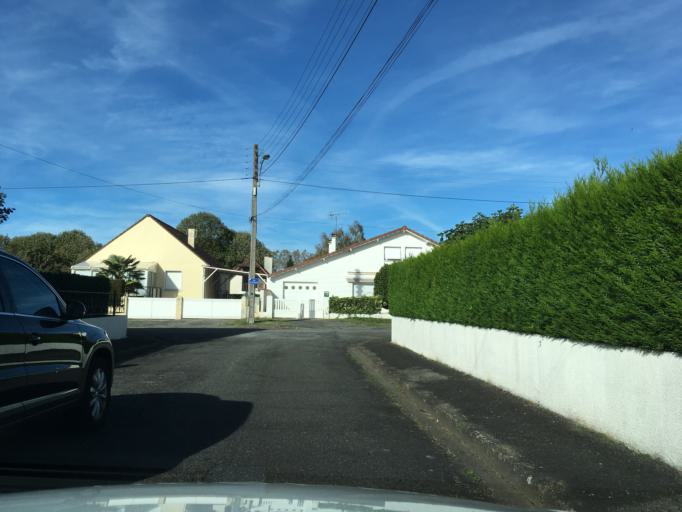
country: FR
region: Aquitaine
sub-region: Departement des Pyrenees-Atlantiques
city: Lons
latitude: 43.3315
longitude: -0.3762
